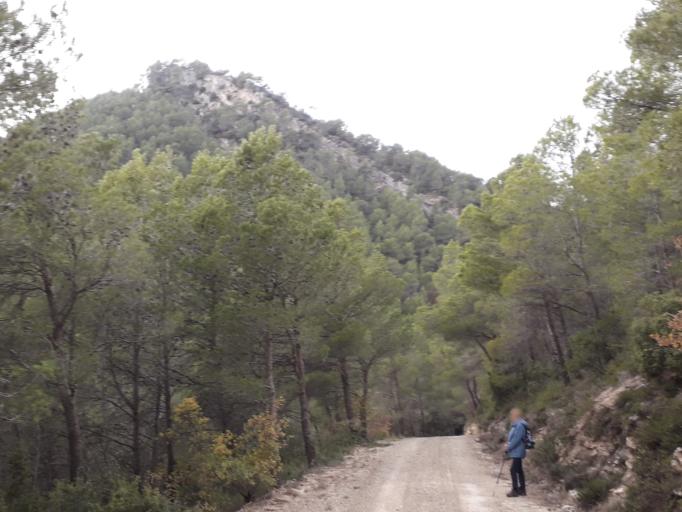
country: ES
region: Catalonia
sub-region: Provincia de Barcelona
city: Sant Marti de Tous
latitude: 41.5215
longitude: 1.5114
